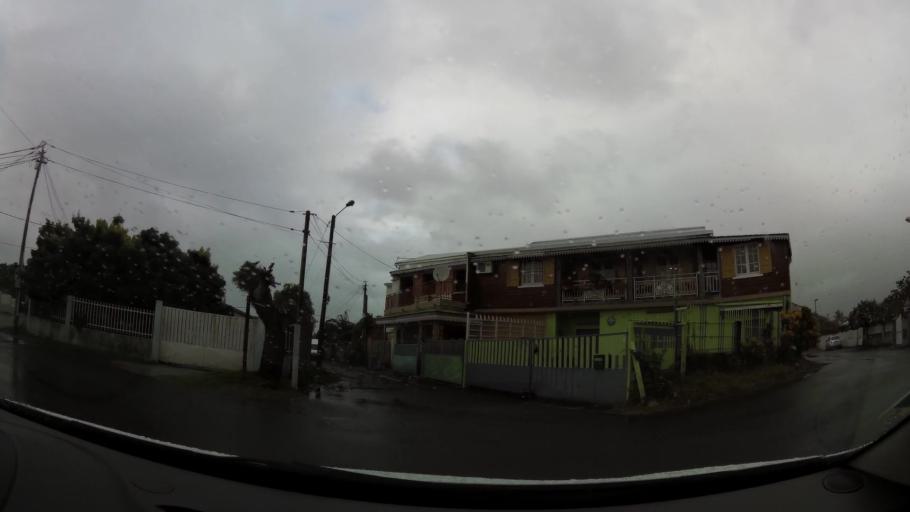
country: RE
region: Reunion
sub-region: Reunion
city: Saint-Andre
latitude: -20.9744
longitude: 55.6528
